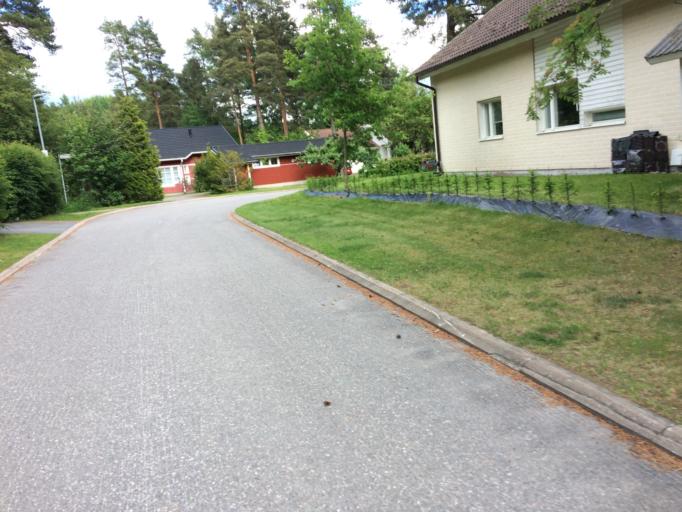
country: FI
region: Varsinais-Suomi
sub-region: Turku
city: Turku
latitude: 60.4690
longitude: 22.3172
